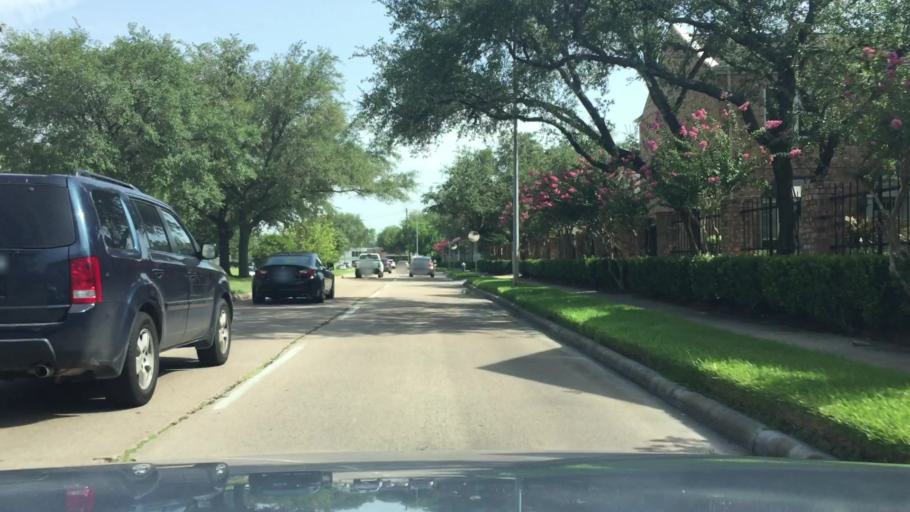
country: US
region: Texas
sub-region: Harris County
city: Bunker Hill Village
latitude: 29.7588
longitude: -95.5765
